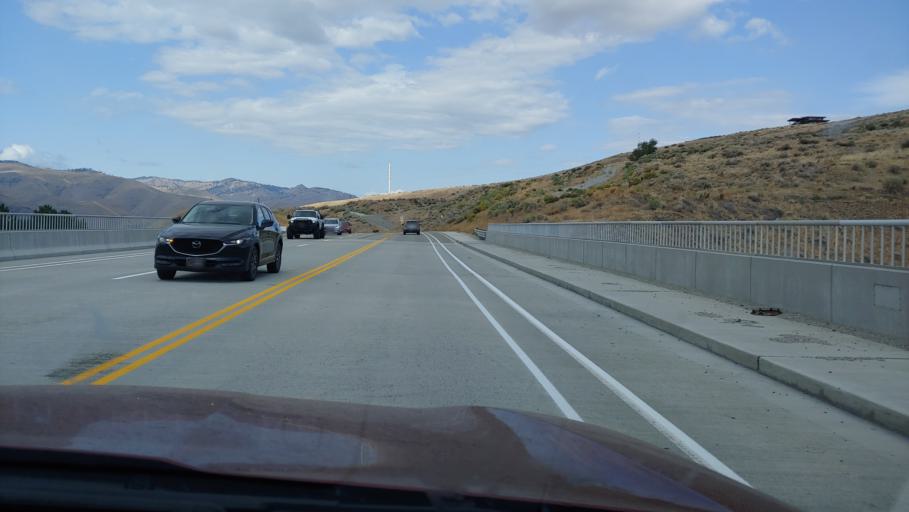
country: US
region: Washington
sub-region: Douglas County
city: East Wenatchee Bench
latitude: 47.4583
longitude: -120.2907
